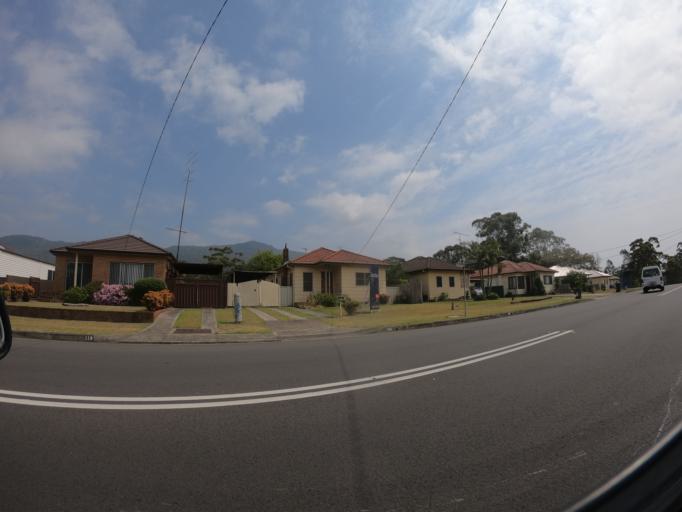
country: AU
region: New South Wales
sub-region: Wollongong
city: Fairy Meadow
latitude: -34.3835
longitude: 150.8864
